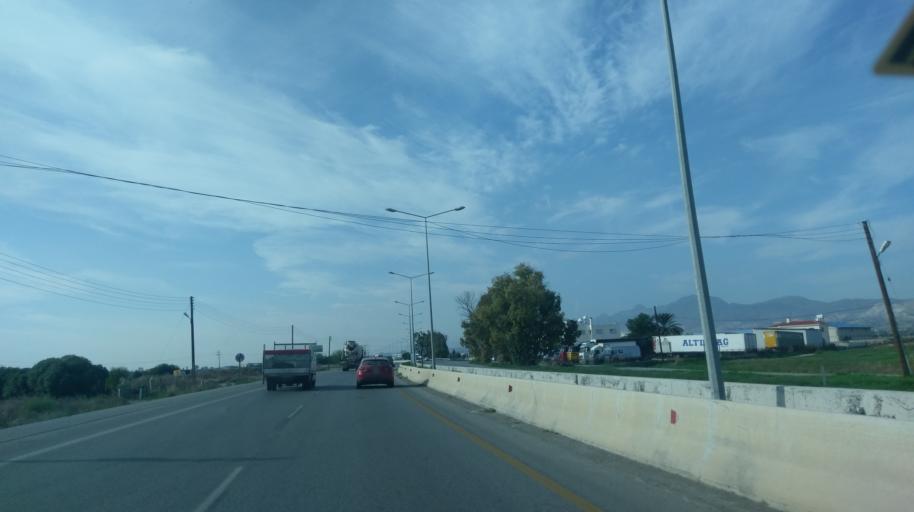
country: CY
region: Lefkosia
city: Geri
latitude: 35.2147
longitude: 33.5139
